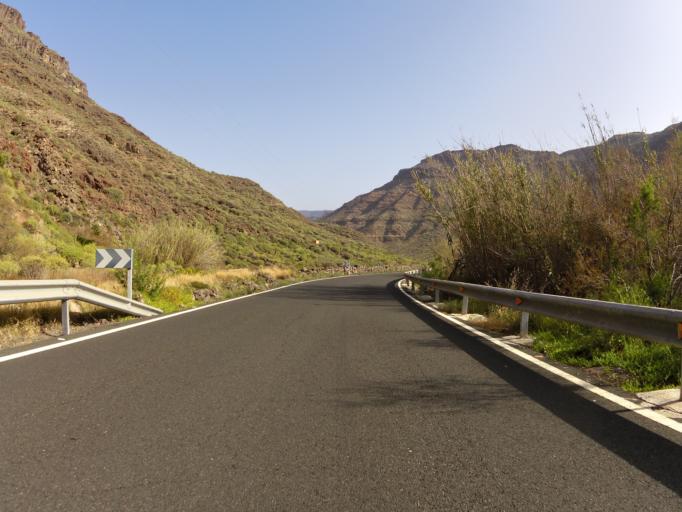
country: ES
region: Canary Islands
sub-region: Provincia de Las Palmas
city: Puerto Rico
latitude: 27.8099
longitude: -15.6674
